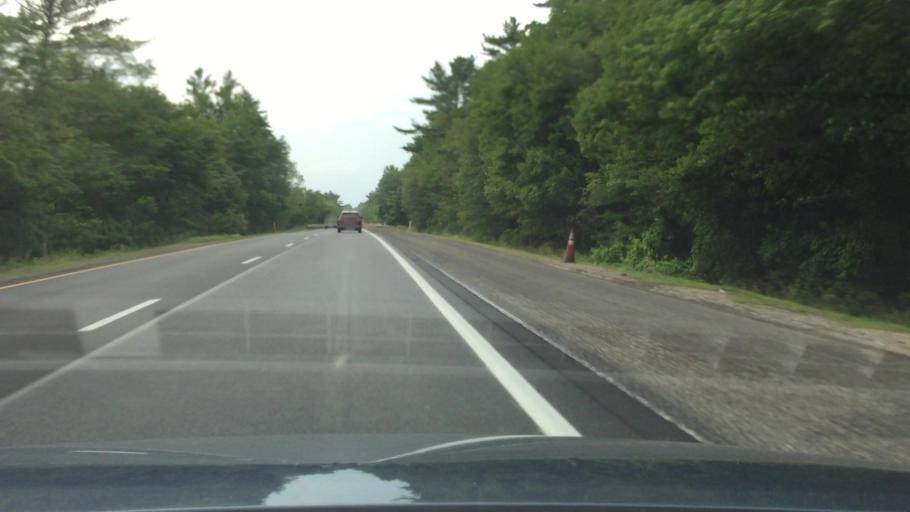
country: US
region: Massachusetts
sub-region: Plymouth County
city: Marshfield
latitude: 42.0733
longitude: -70.7334
